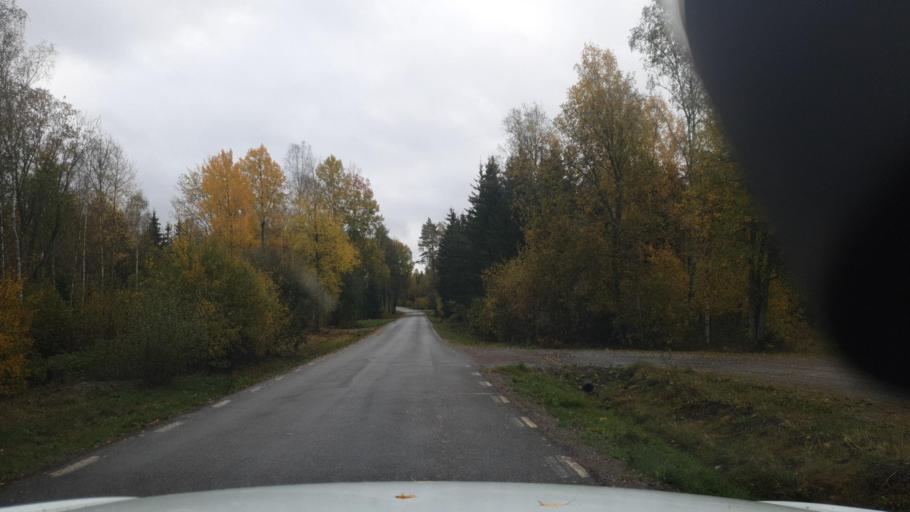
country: SE
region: Vaermland
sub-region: Karlstads Kommun
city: Valberg
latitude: 59.4174
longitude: 13.1213
